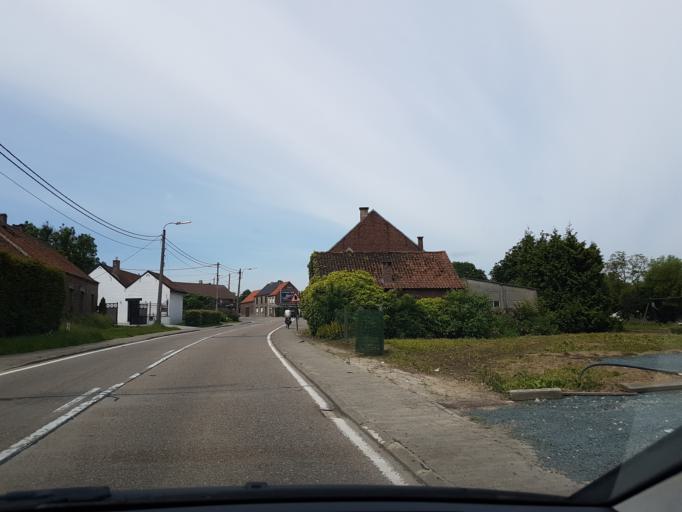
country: BE
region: Flanders
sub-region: Provincie Vlaams-Brabant
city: Asse
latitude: 50.8976
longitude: 4.1774
